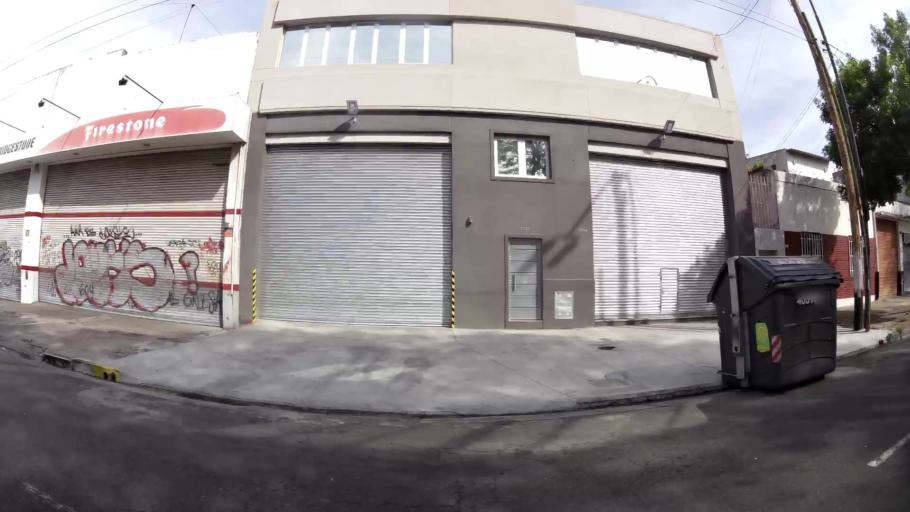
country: AR
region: Buenos Aires F.D.
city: Villa Lugano
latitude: -34.6544
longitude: -58.4953
